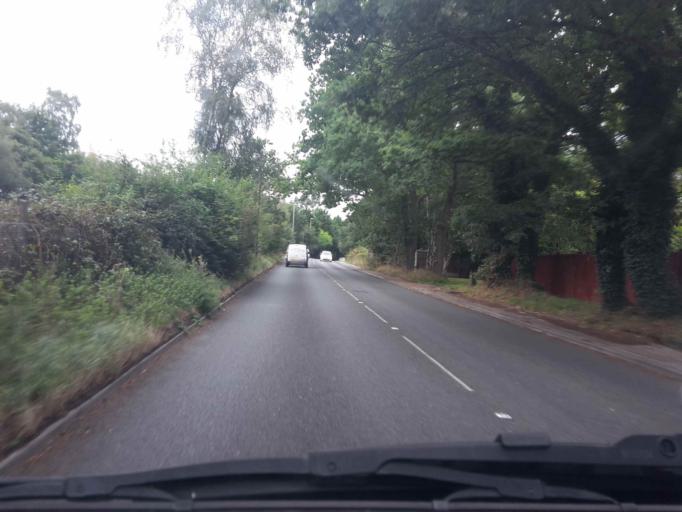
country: GB
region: England
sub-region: Hampshire
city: Fleet
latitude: 51.2919
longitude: -0.8178
